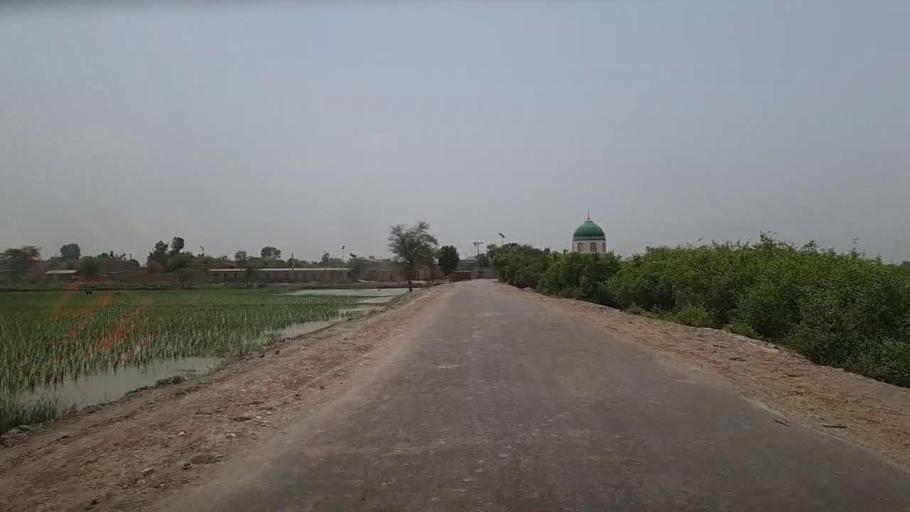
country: PK
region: Sindh
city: Sita Road
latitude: 27.0622
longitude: 67.9037
